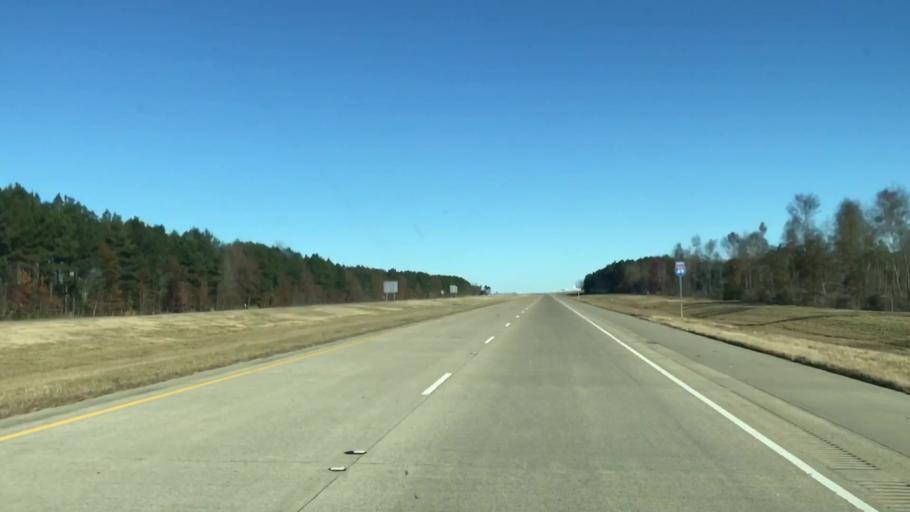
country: US
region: Louisiana
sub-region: Caddo Parish
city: Blanchard
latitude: 32.6041
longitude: -93.8329
